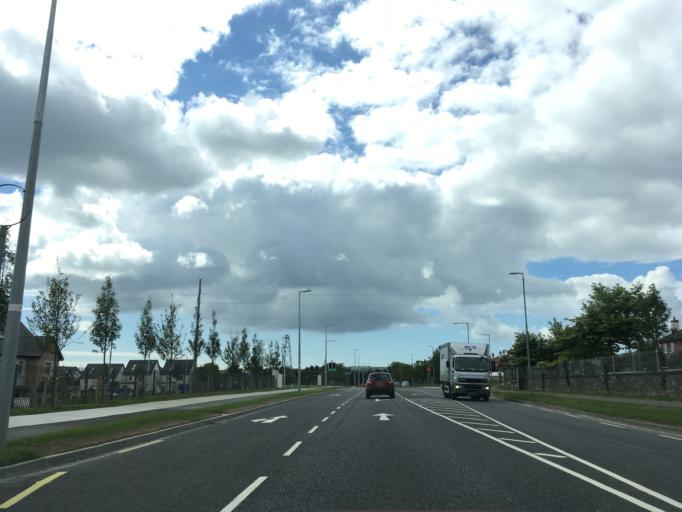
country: IE
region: Munster
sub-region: County Cork
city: Carrigaline
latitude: 51.8284
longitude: -8.3961
